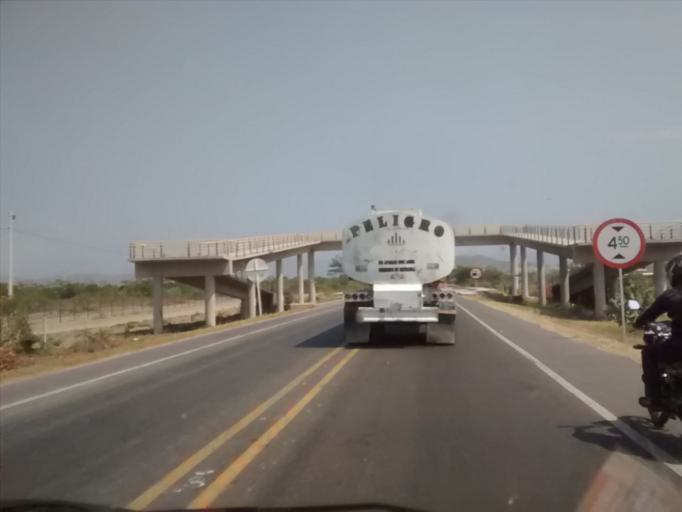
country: CO
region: Magdalena
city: Santa Marta
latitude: 11.1980
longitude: -74.1847
